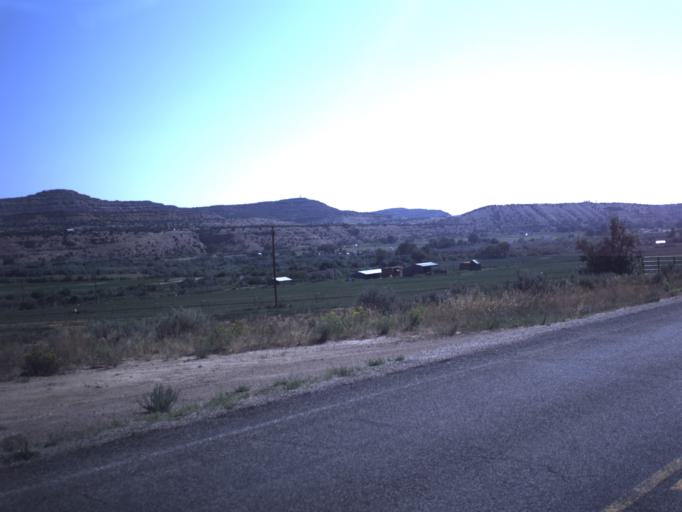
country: US
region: Utah
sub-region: Duchesne County
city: Duchesne
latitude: 40.2748
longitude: -110.4605
